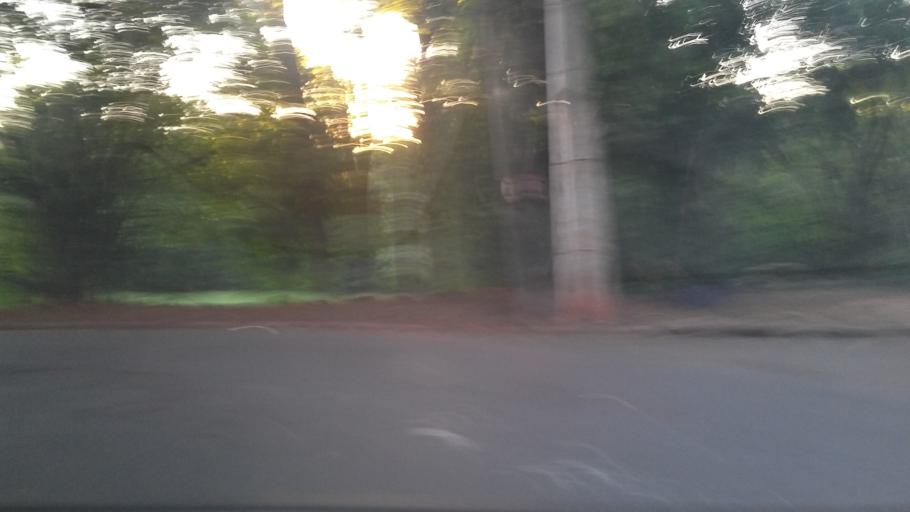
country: BR
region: Parana
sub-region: Londrina
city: Londrina
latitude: -23.3208
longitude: -51.1717
